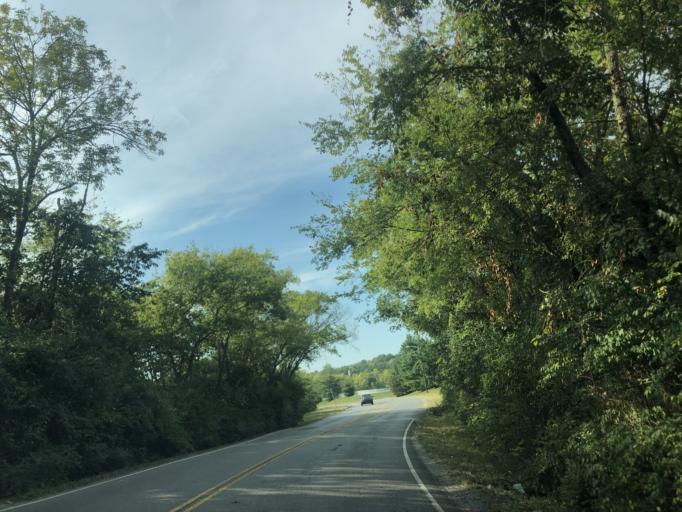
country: US
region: Tennessee
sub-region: Davidson County
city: Oak Hill
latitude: 36.0799
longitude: -86.6781
